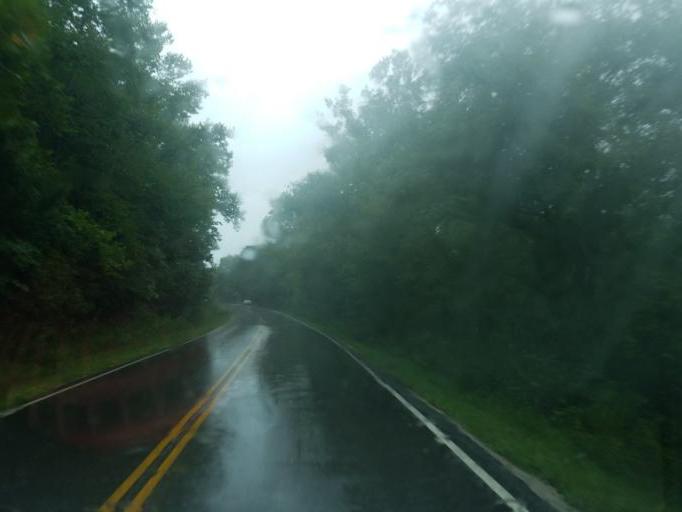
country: US
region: Kentucky
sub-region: Carter County
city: Grayson
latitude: 38.4914
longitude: -83.0231
